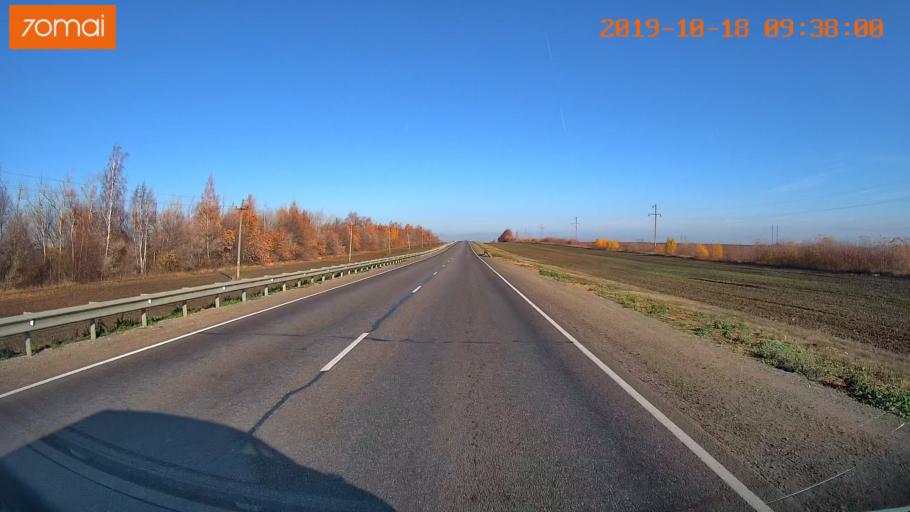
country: RU
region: Tula
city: Yefremov
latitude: 53.2312
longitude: 38.1388
